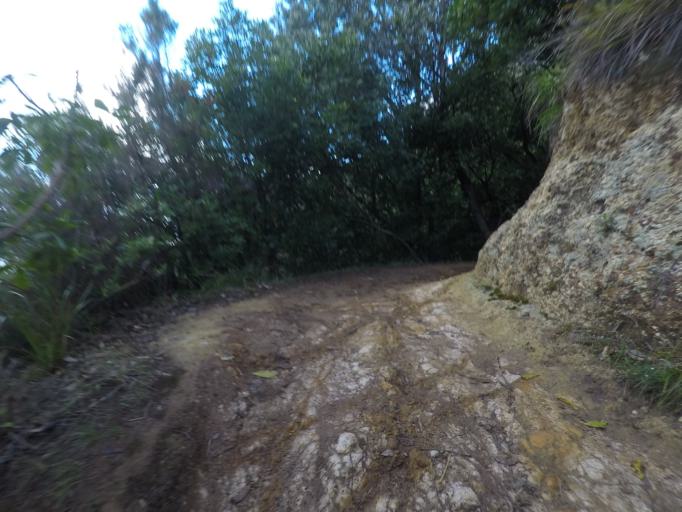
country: NZ
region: Bay of Plenty
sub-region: Western Bay of Plenty District
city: Waihi Beach
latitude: -37.3880
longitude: 175.9422
